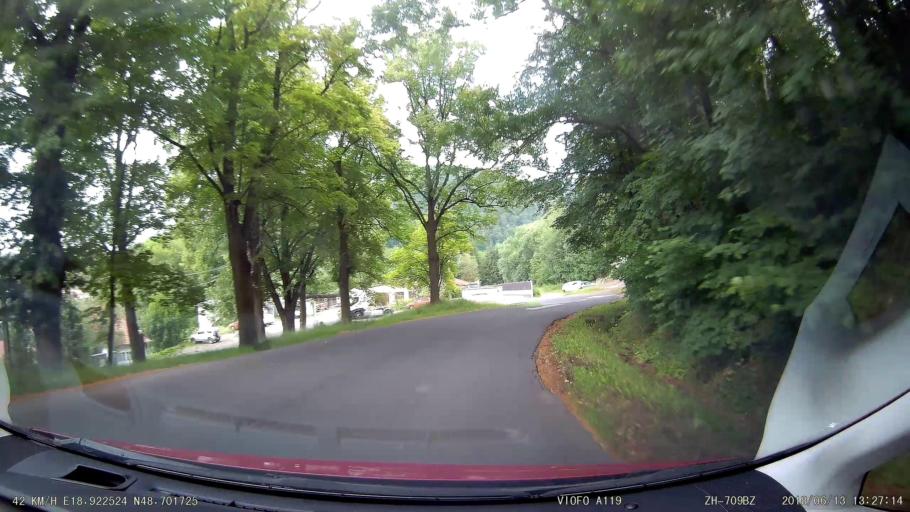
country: SK
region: Banskobystricky
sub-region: Okres Ziar nad Hronom
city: Kremnica
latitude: 48.7018
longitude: 18.9226
